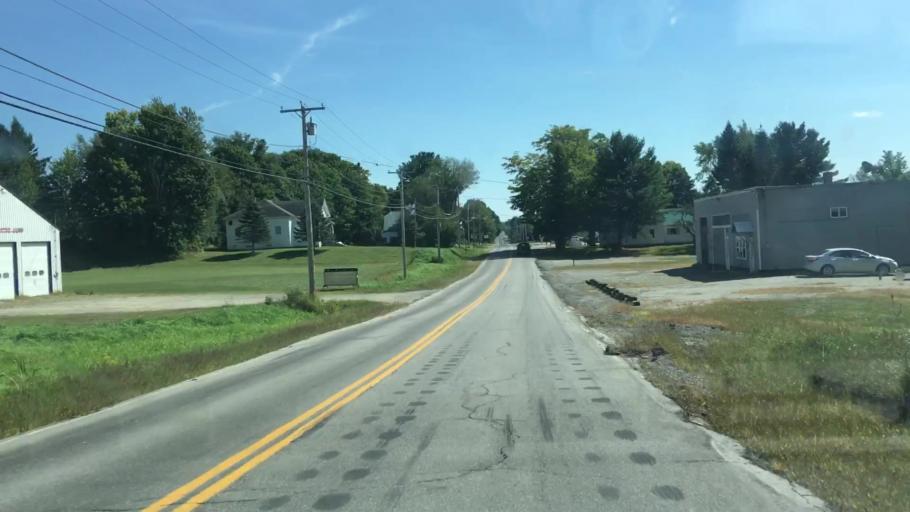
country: US
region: Maine
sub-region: Penobscot County
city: Bradford
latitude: 45.1686
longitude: -68.8465
